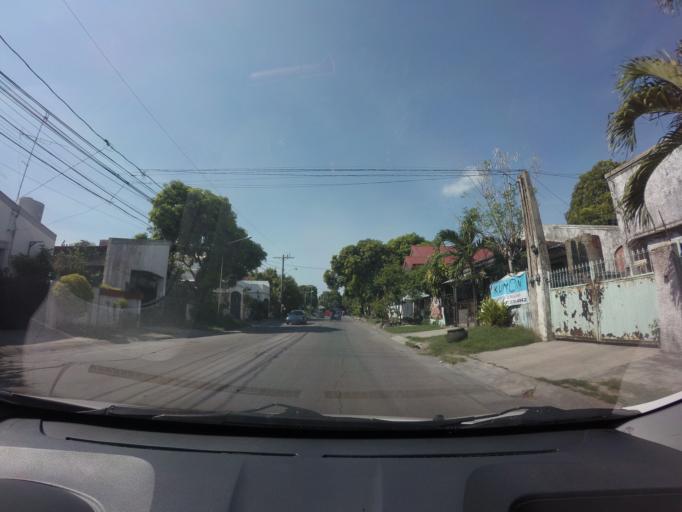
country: PH
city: Sambayanihan People's Village
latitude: 14.4450
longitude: 121.0074
